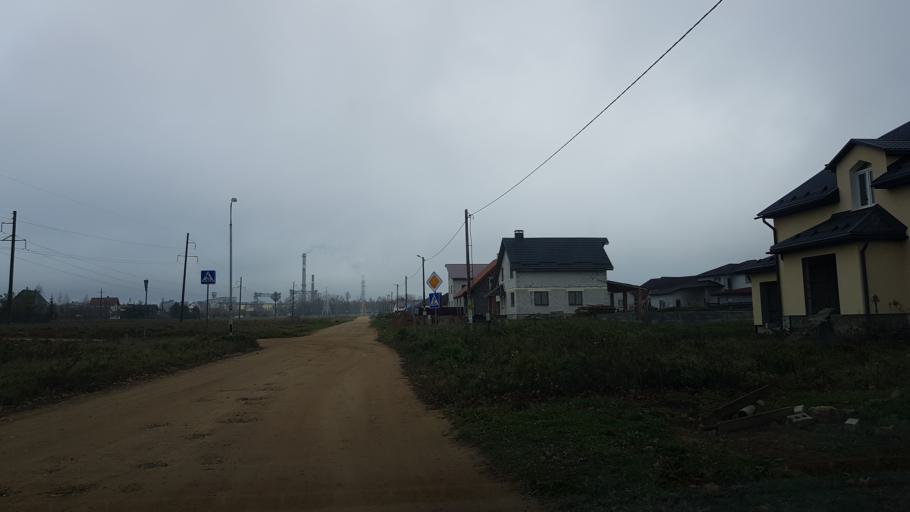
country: BY
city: Fanipol
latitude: 53.7304
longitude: 27.3183
